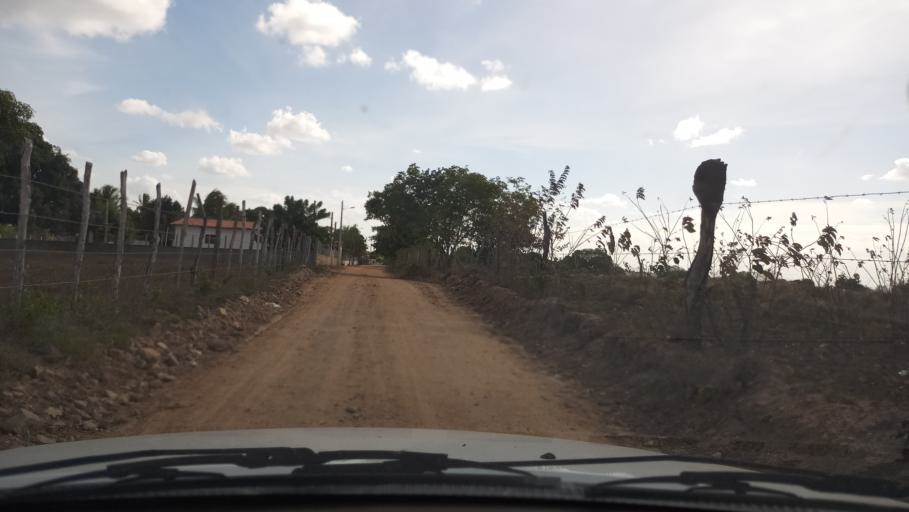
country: BR
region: Rio Grande do Norte
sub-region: Goianinha
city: Goianinha
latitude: -6.3172
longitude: -35.3076
